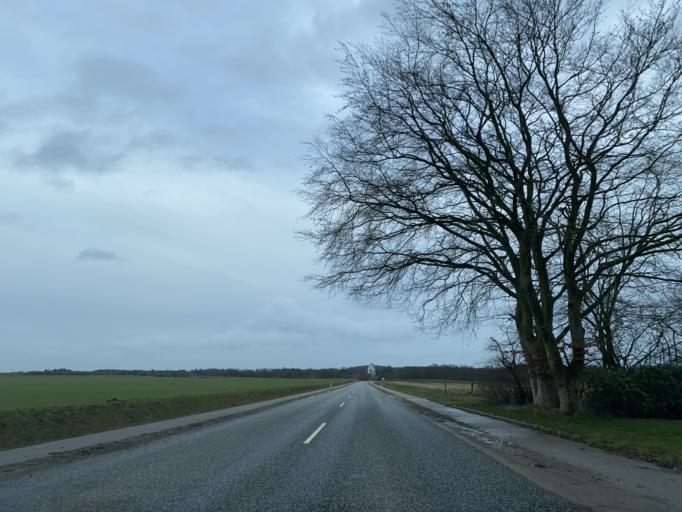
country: DK
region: Central Jutland
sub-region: Viborg Kommune
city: Bjerringbro
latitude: 56.2808
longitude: 9.6138
